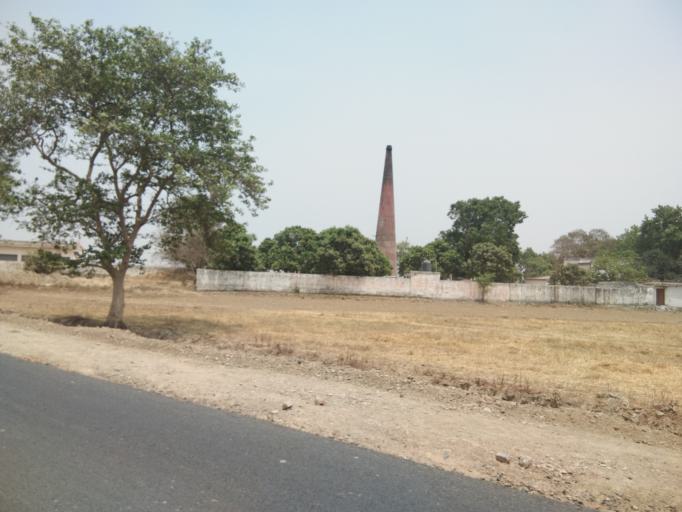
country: IN
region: Uttar Pradesh
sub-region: Ghazipur
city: Zamania
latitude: 25.4356
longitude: 83.6798
